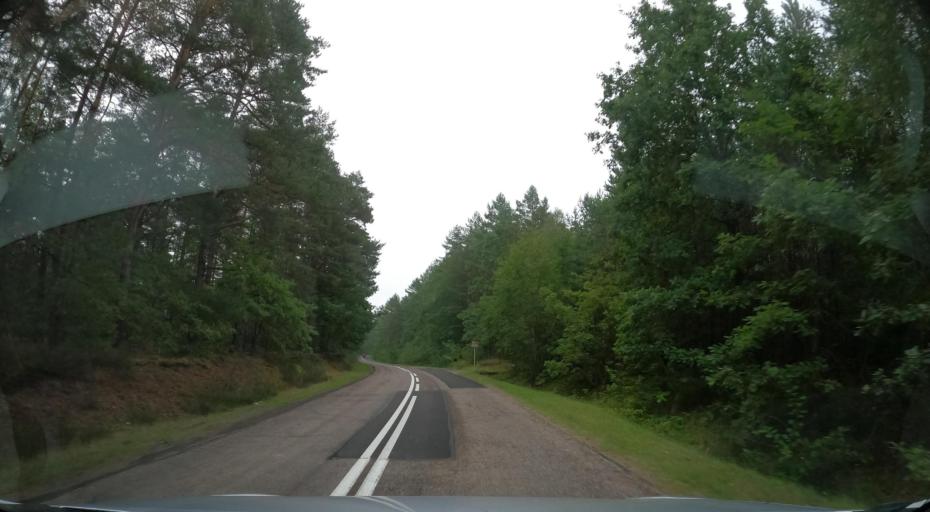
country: PL
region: Pomeranian Voivodeship
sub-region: Powiat wejherowski
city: Linia
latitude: 54.4655
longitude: 17.9922
